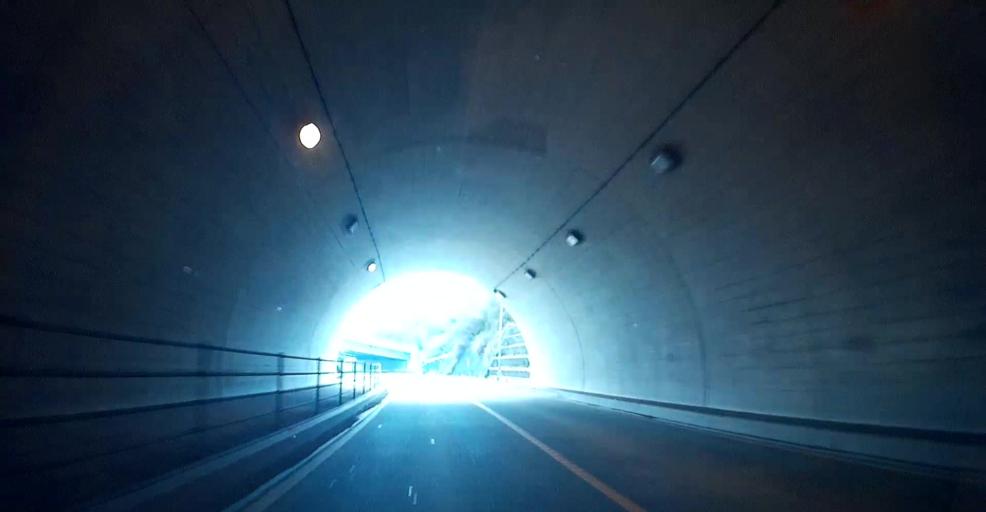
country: JP
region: Kumamoto
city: Yatsushiro
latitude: 32.6073
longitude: 130.4412
